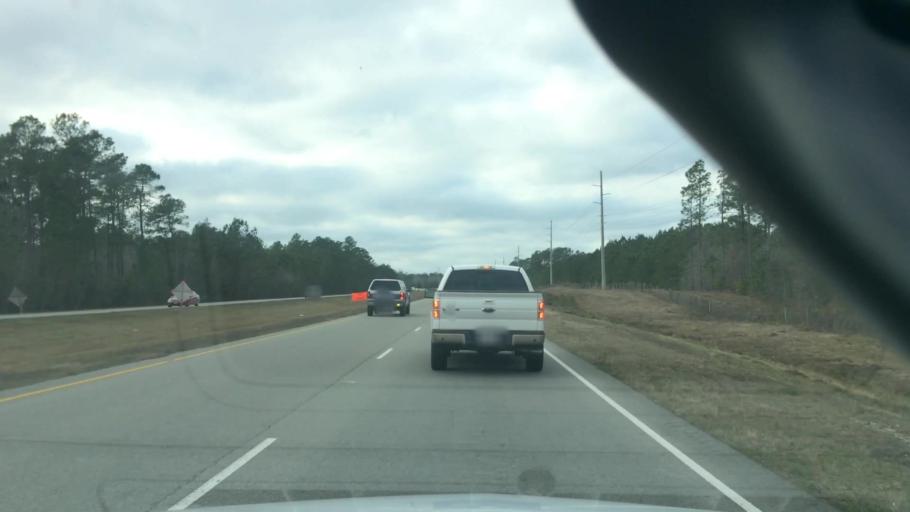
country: US
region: North Carolina
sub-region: Brunswick County
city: Shallotte
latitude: 33.9887
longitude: -78.3774
